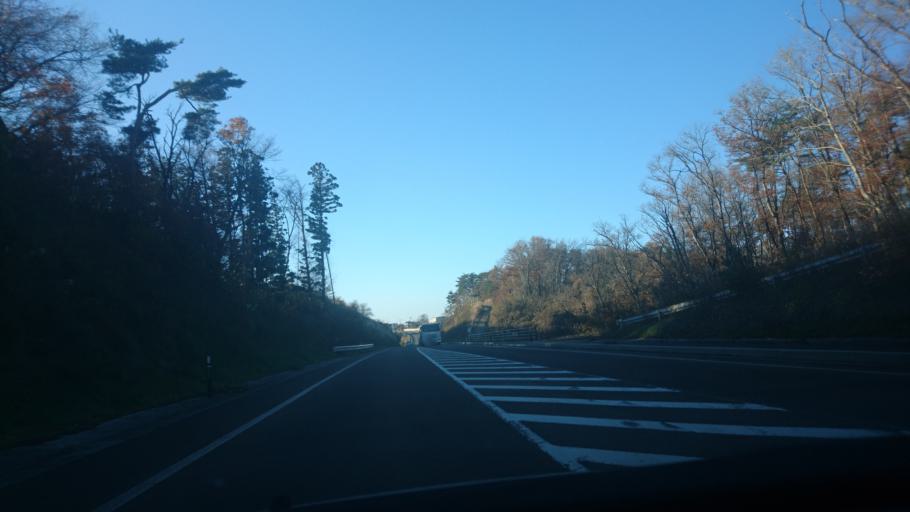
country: JP
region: Iwate
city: Ichinoseki
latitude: 38.9052
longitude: 141.1725
